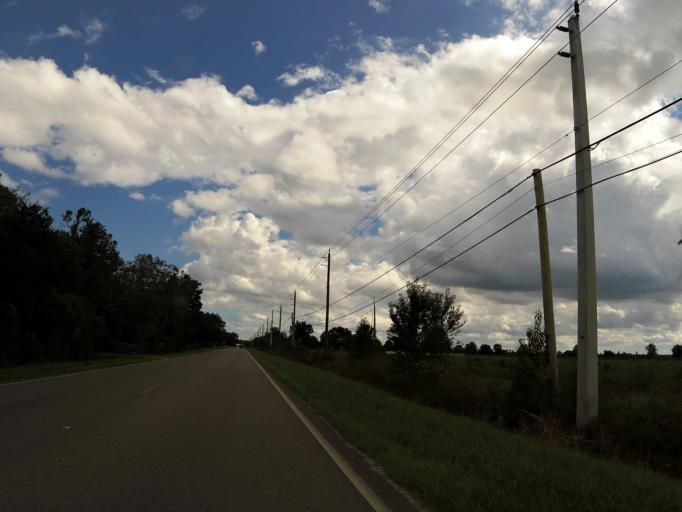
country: US
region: Florida
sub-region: Saint Johns County
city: Saint Augustine South
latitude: 29.8335
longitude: -81.4982
